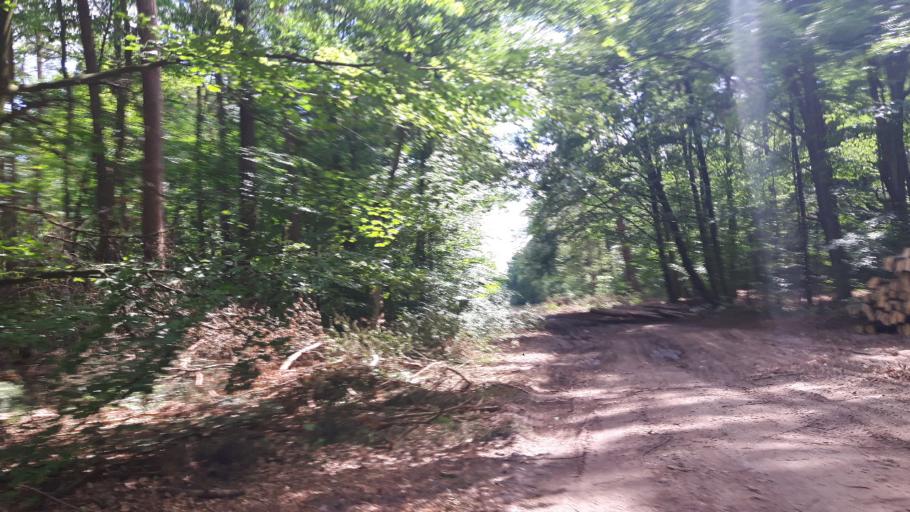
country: PL
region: West Pomeranian Voivodeship
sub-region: Powiat goleniowski
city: Osina
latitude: 53.6441
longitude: 14.9245
